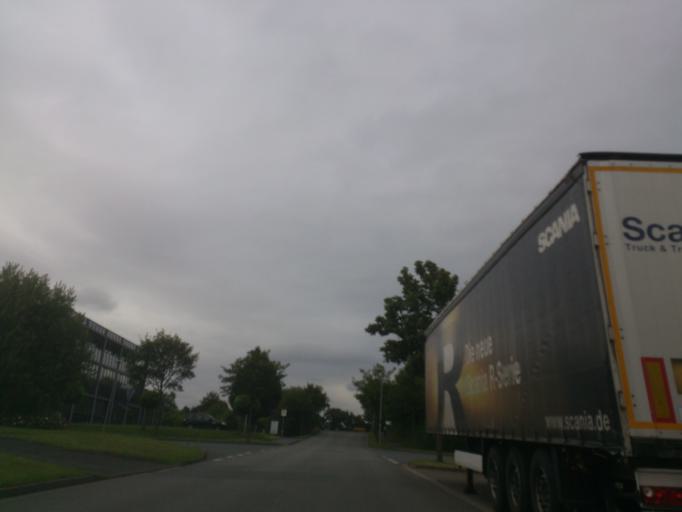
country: DE
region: North Rhine-Westphalia
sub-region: Regierungsbezirk Detmold
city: Paderborn
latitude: 51.7257
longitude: 8.7981
